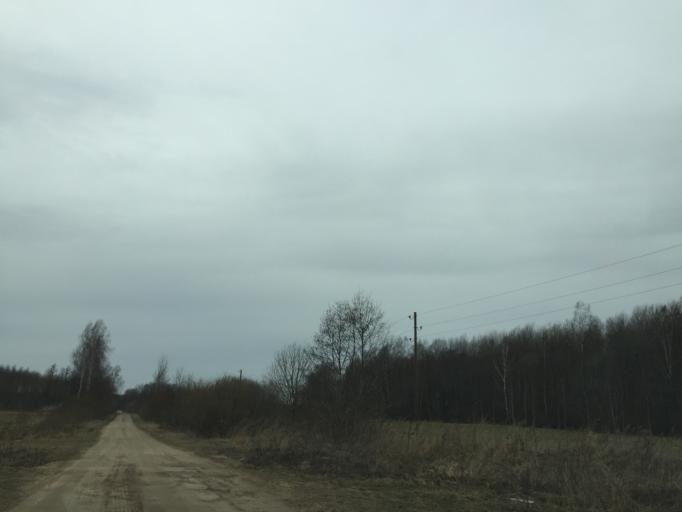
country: LV
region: Ilukste
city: Ilukste
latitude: 56.0313
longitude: 26.2872
